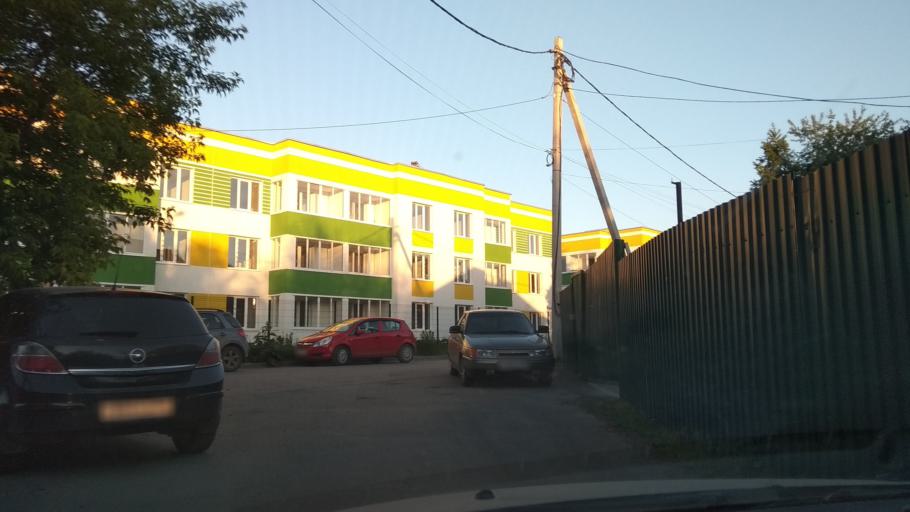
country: RU
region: Sverdlovsk
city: Sredneuralsk
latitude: 56.9914
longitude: 60.4574
